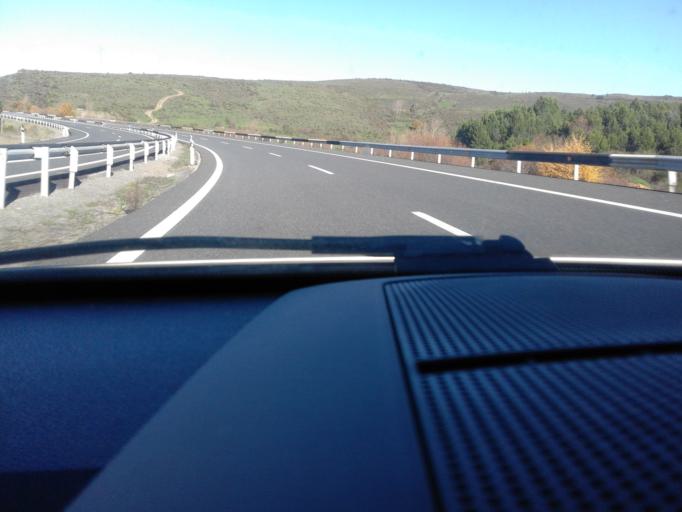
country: ES
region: Castille and Leon
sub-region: Provincia de Leon
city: Carrocera
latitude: 42.7496
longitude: -5.7702
